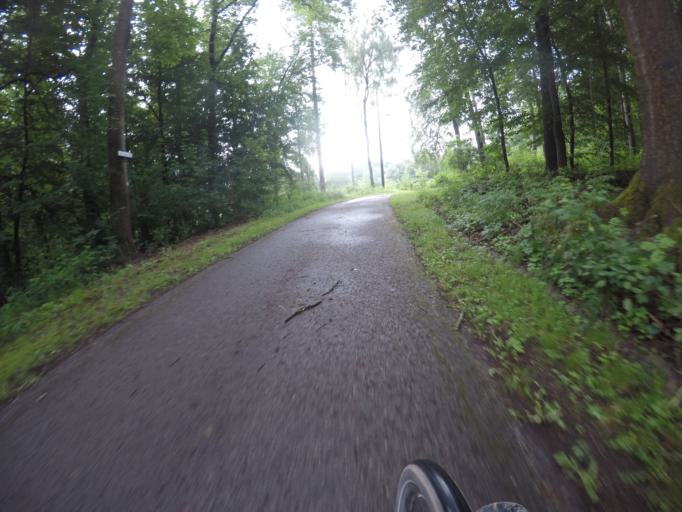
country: DE
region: Baden-Wuerttemberg
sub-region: Regierungsbezirk Stuttgart
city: Sindelfingen
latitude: 48.7151
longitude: 9.0525
